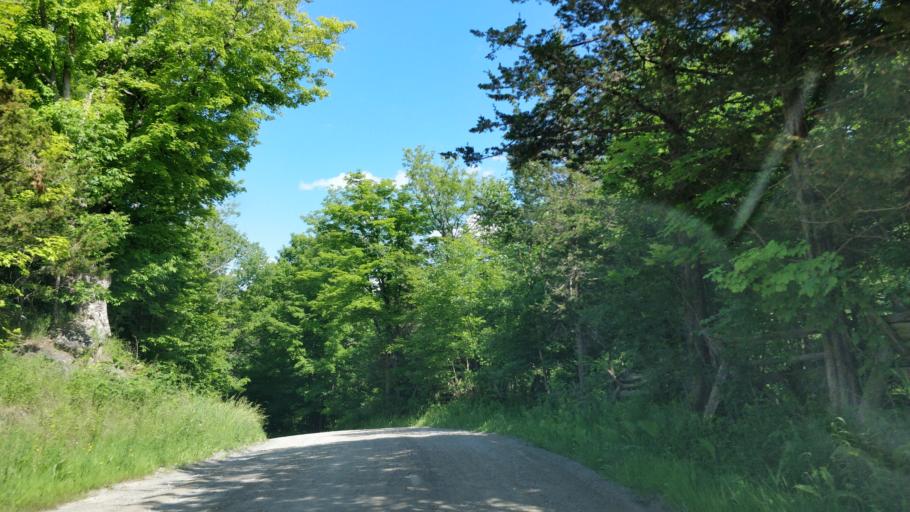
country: CA
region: Ontario
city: Perth
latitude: 44.6799
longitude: -76.5312
